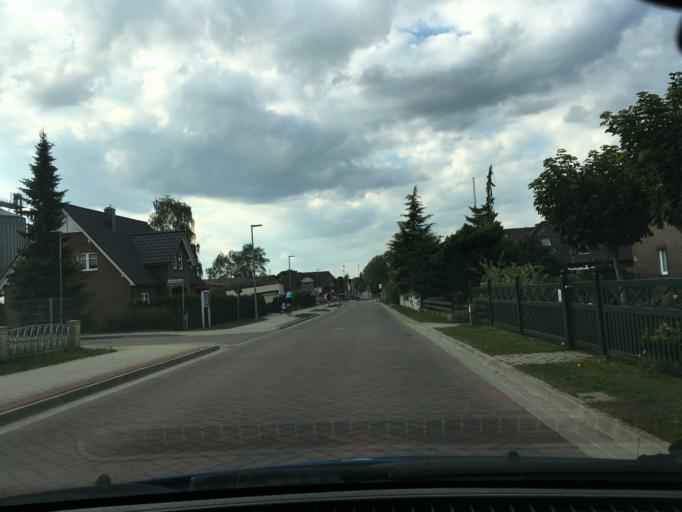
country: DE
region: Lower Saxony
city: Wulfsen
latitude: 53.2921
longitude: 10.1477
